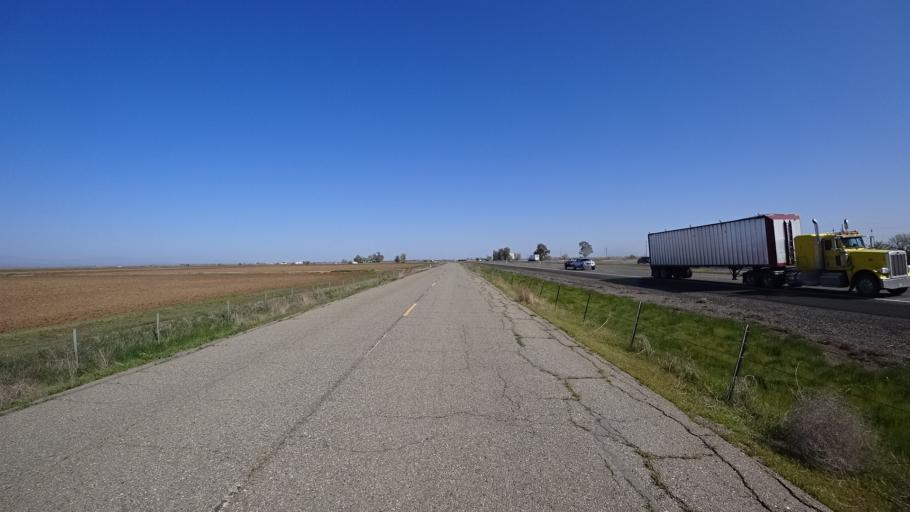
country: US
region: California
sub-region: Glenn County
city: Willows
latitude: 39.4532
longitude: -122.1940
